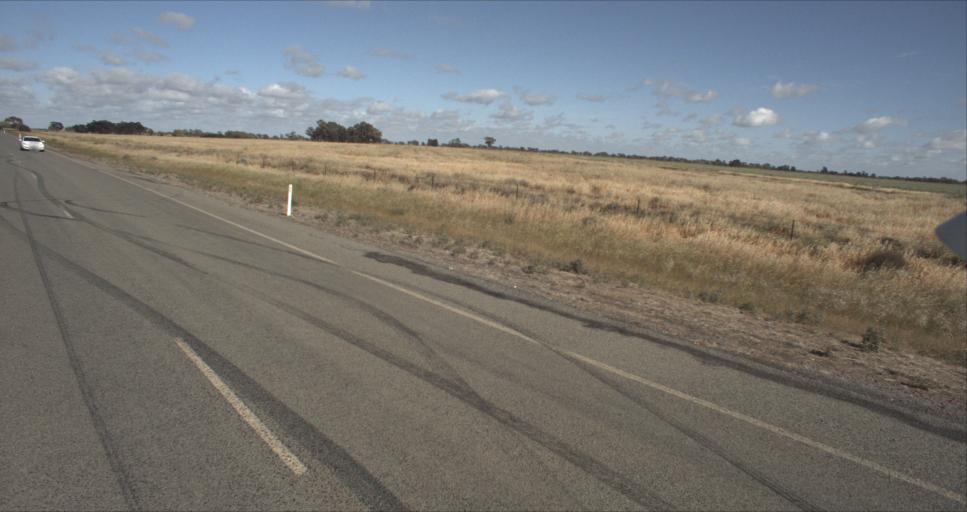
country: AU
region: New South Wales
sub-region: Leeton
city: Leeton
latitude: -34.5537
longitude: 146.2904
